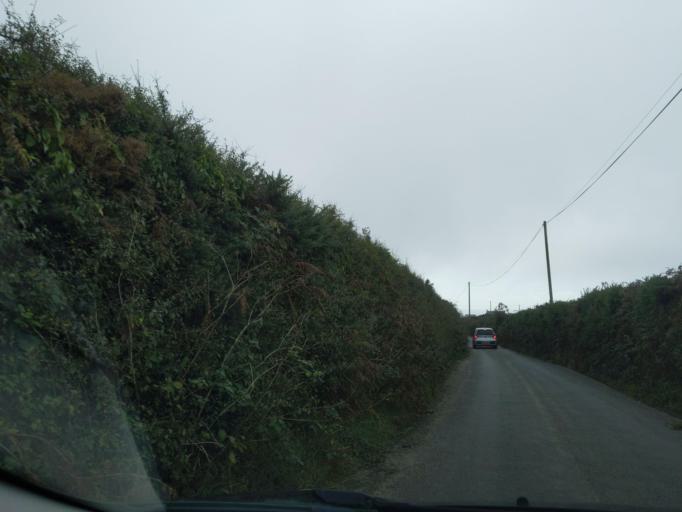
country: GB
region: England
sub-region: Cornwall
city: Germoe
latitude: 50.1020
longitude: -5.3586
